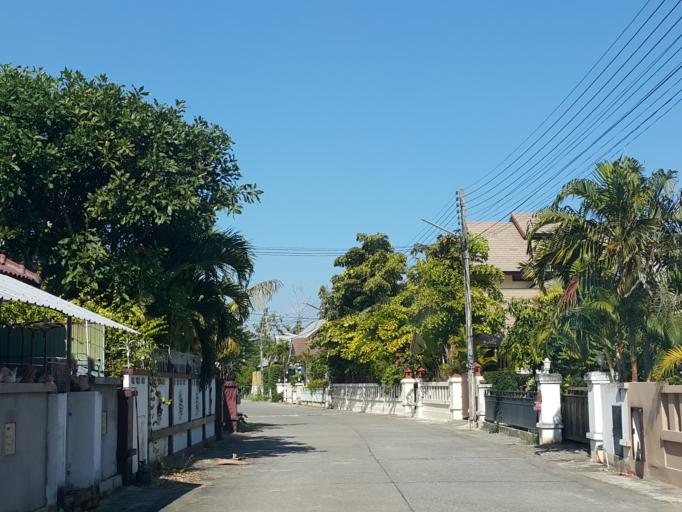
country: TH
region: Chiang Mai
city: San Sai
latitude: 18.8739
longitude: 99.0079
